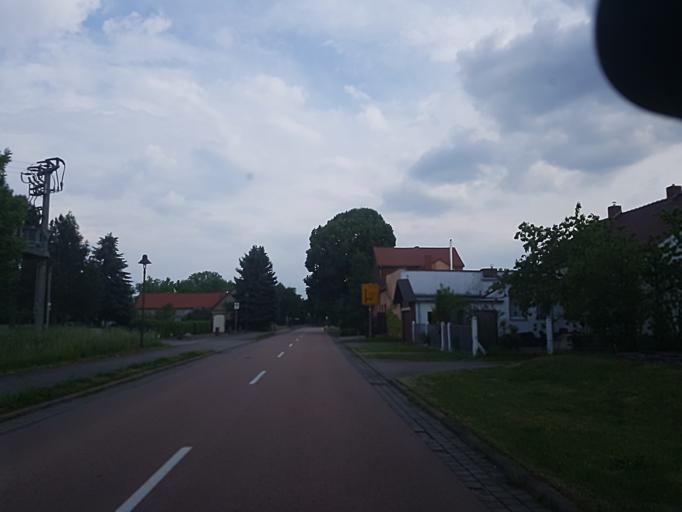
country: DE
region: Saxony-Anhalt
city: Klieken
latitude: 51.9292
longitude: 12.3799
